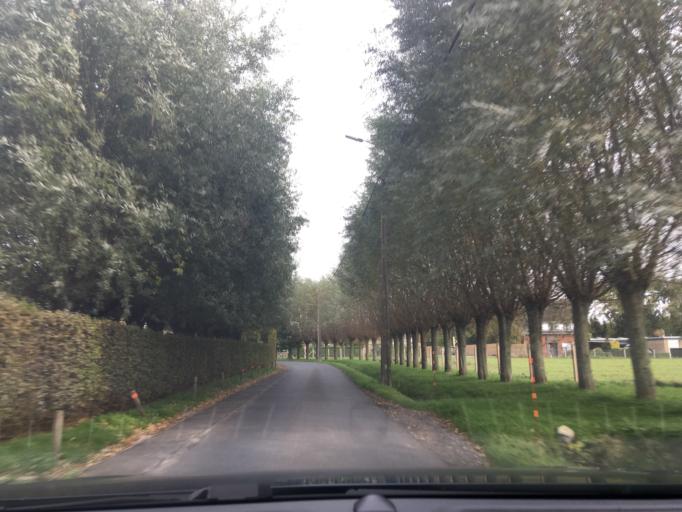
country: BE
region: Flanders
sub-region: Provincie West-Vlaanderen
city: Roeselare
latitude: 50.9138
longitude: 3.1041
